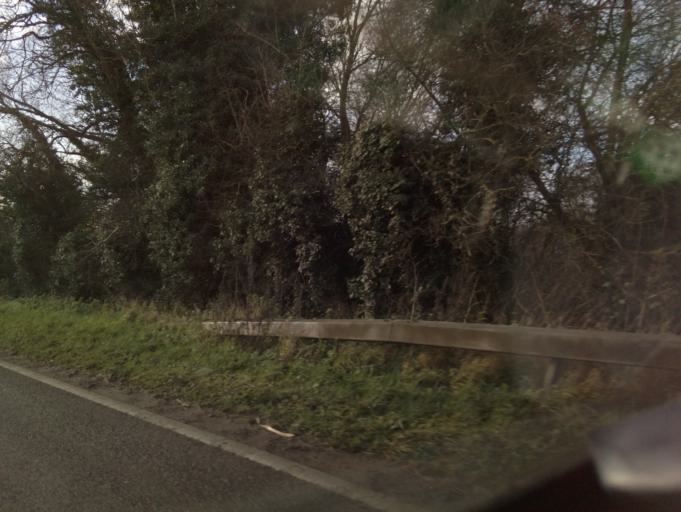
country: GB
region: England
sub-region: Warwickshire
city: Curdworth
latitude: 52.5700
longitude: -1.7632
